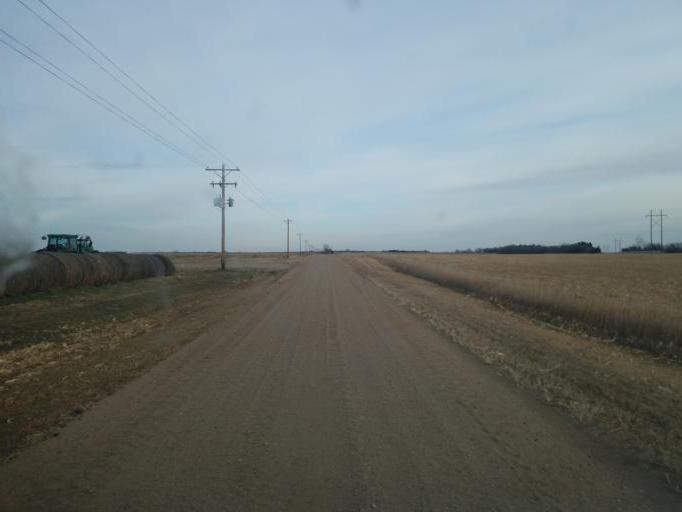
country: US
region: Nebraska
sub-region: Holt County
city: O'Neill
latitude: 42.4369
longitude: -98.3149
